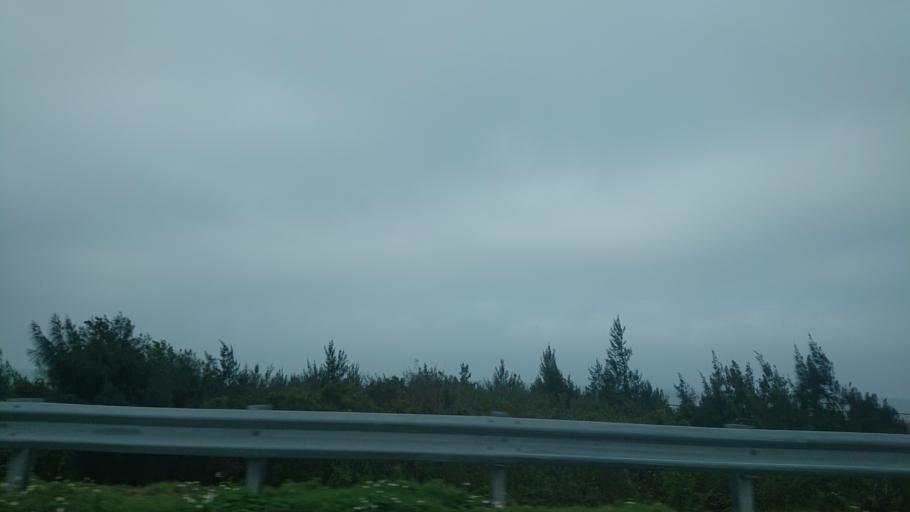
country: TW
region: Taiwan
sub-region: Miaoli
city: Miaoli
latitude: 24.5235
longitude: 120.6884
